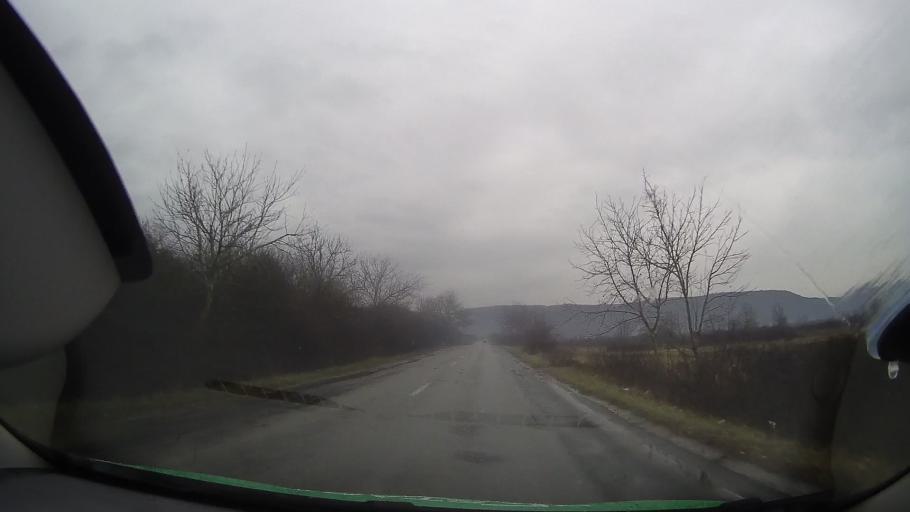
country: RO
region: Bihor
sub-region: Comuna Sambata
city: Sambata
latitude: 46.7799
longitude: 22.1876
